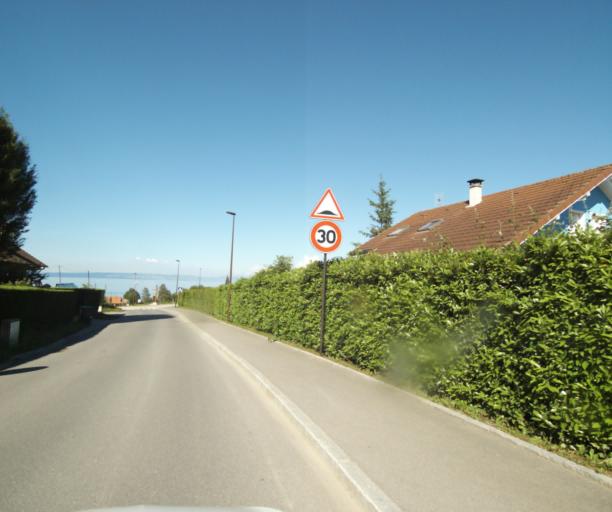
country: FR
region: Rhone-Alpes
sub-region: Departement de la Haute-Savoie
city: Sciez
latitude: 46.3542
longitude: 6.3485
